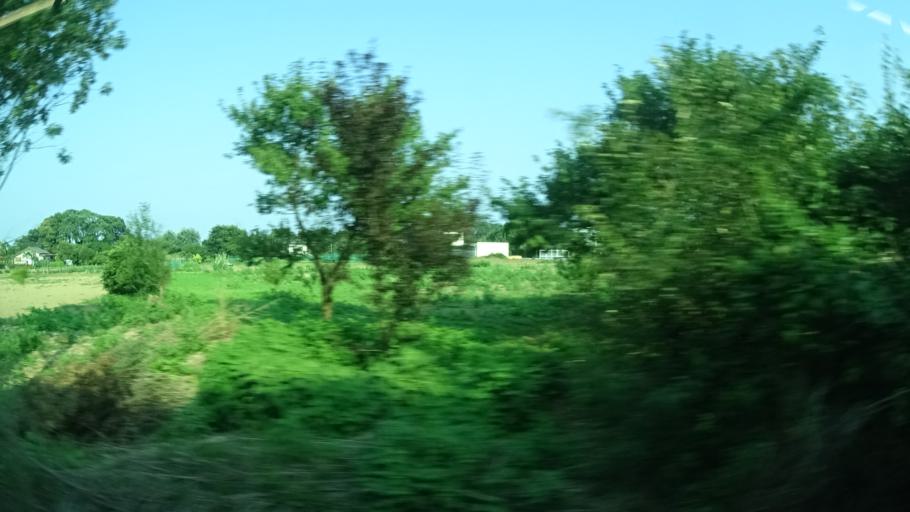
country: JP
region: Ibaraki
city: Takahagi
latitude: 36.7450
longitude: 140.7240
